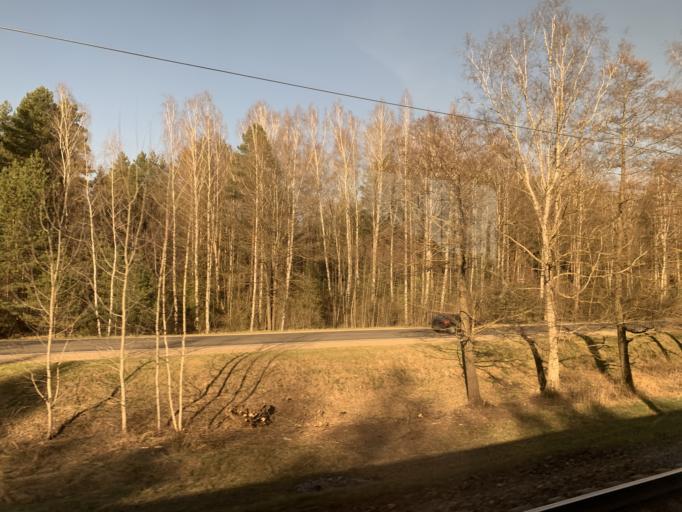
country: BY
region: Grodnenskaya
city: Smarhon'
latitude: 54.4417
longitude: 26.5013
